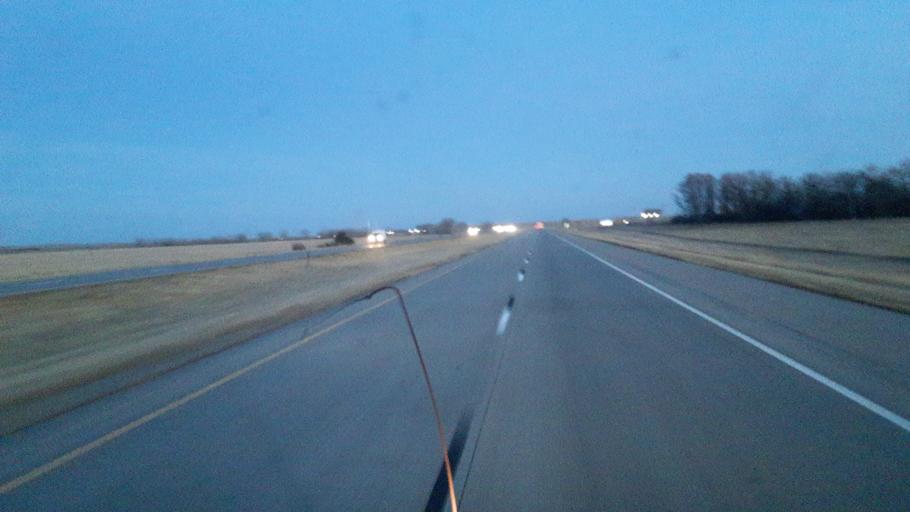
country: US
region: Nebraska
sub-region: Keith County
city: Ogallala
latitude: 41.1067
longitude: -101.4943
